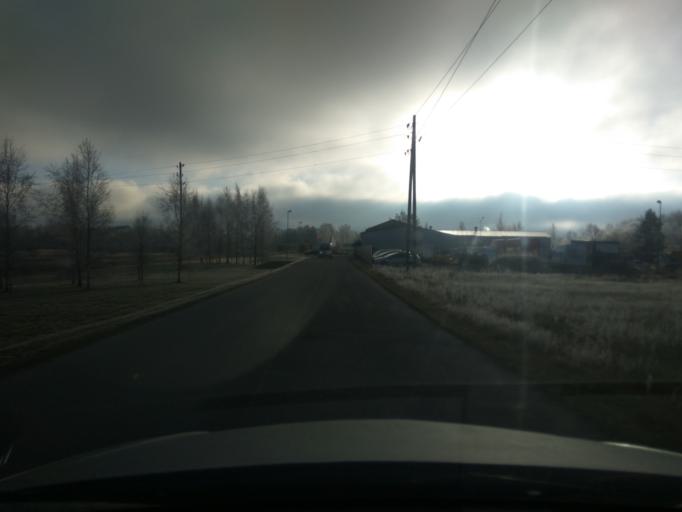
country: LV
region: Kuldigas Rajons
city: Kuldiga
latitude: 56.9674
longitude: 21.9338
